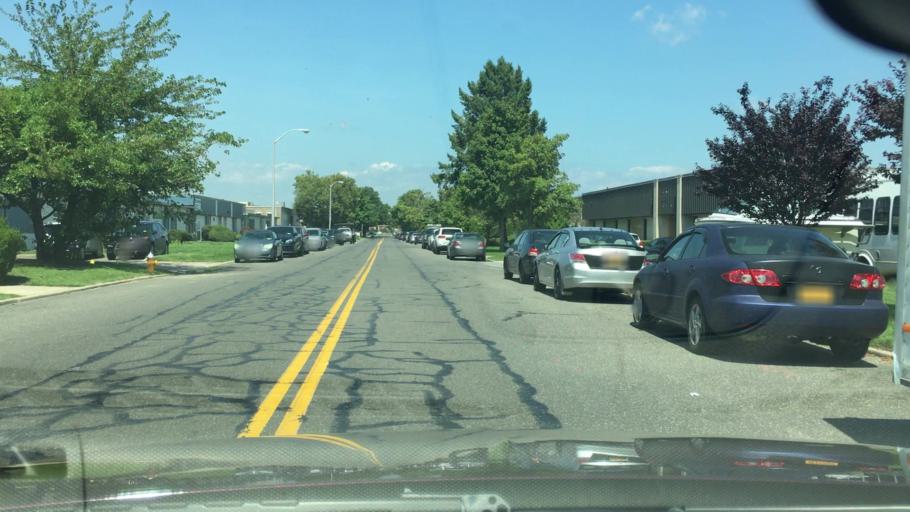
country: US
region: New York
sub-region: Suffolk County
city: Bay Wood
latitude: 40.7623
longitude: -73.2971
